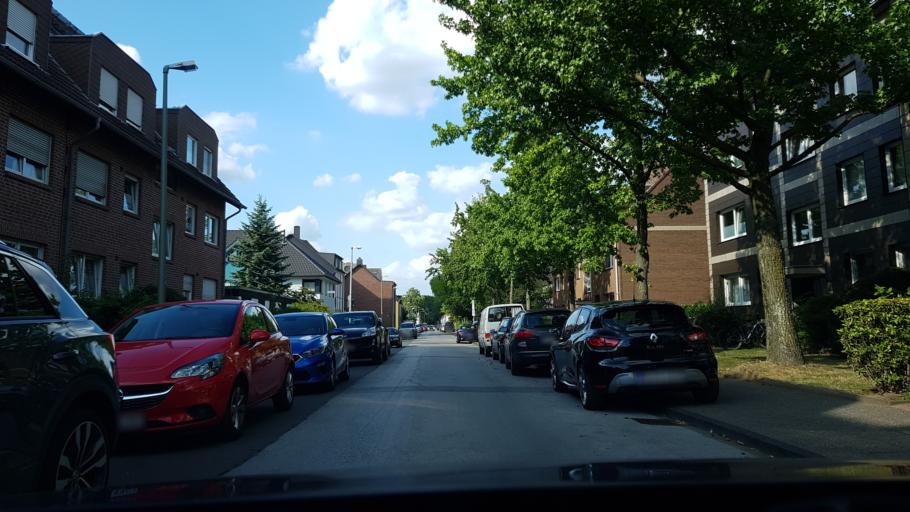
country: DE
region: North Rhine-Westphalia
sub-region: Regierungsbezirk Dusseldorf
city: Hochfeld
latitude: 51.3850
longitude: 6.7677
